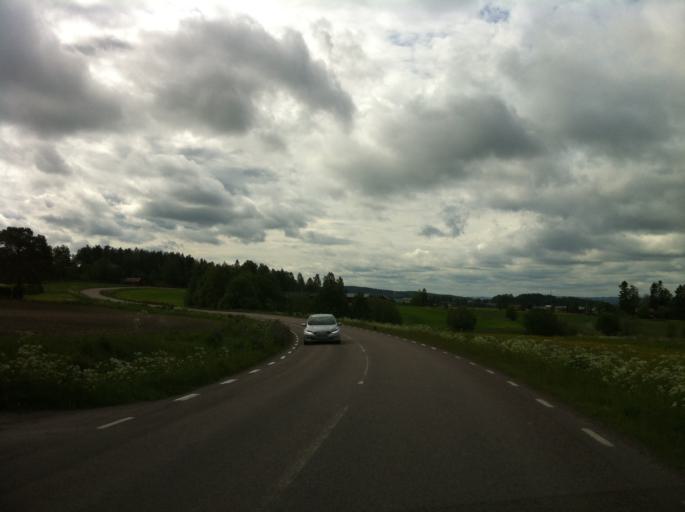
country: SE
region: Vaermland
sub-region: Sunne Kommun
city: Sunne
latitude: 59.8696
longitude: 13.1660
